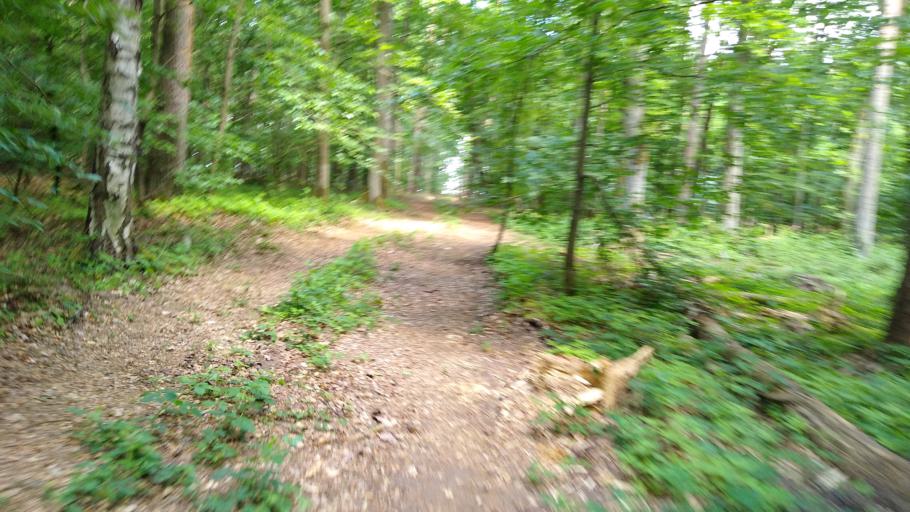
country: DE
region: Bavaria
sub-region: Regierungsbezirk Mittelfranken
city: Seukendorf
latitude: 49.4866
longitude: 10.9049
